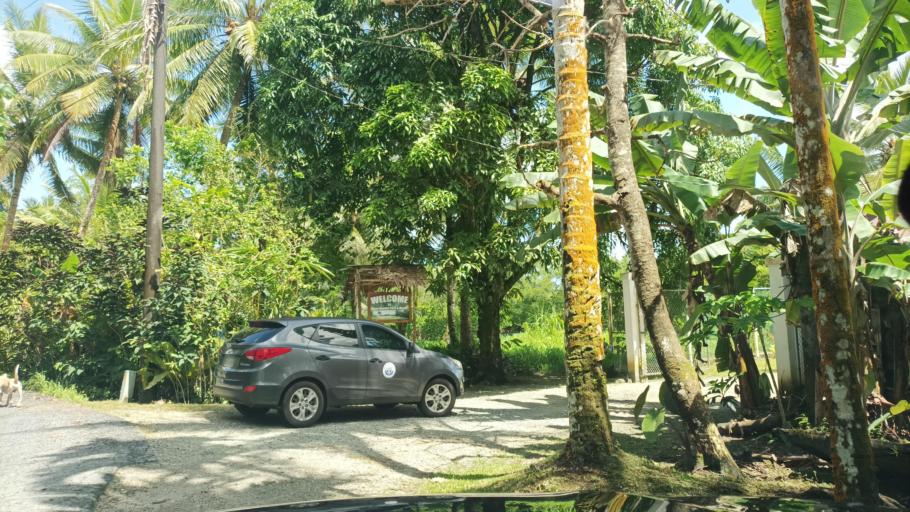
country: FM
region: Pohnpei
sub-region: Sokehs Municipality
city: Palikir - National Government Center
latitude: 6.9400
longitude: 158.1698
